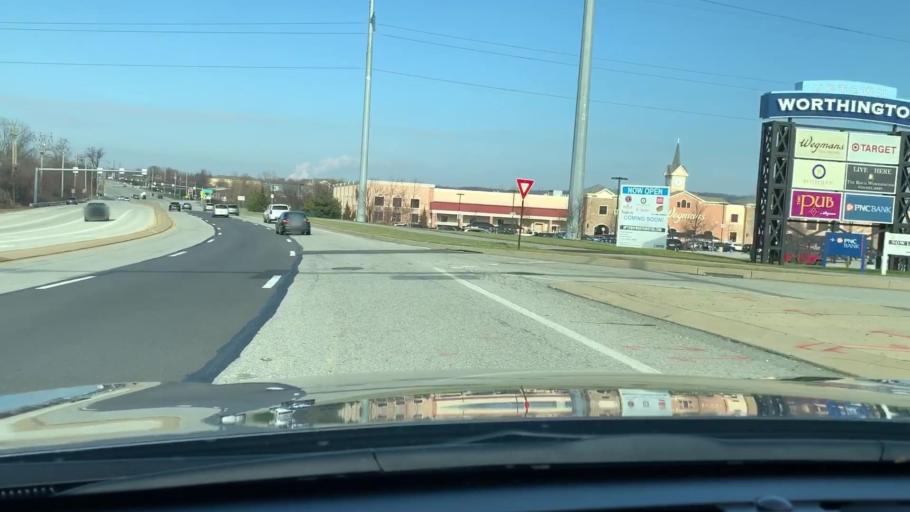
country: US
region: Pennsylvania
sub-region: Chester County
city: Malvern
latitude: 40.0463
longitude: -75.5231
